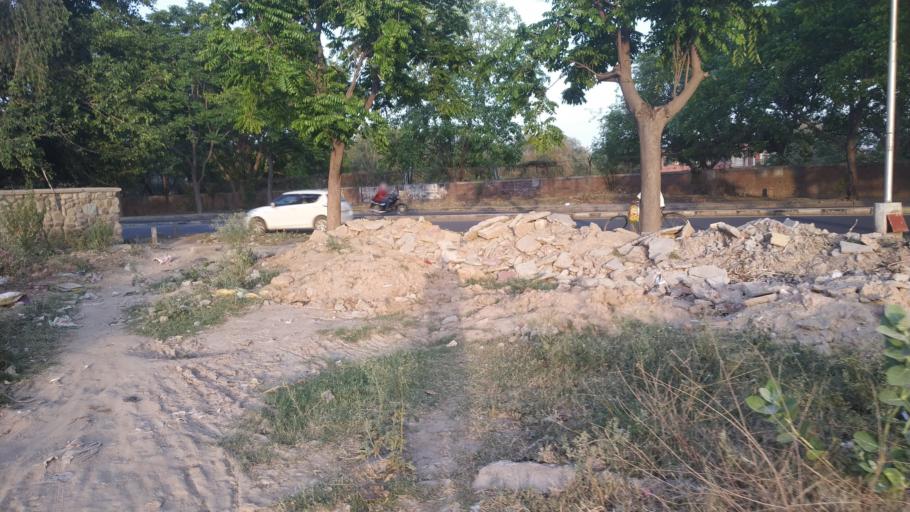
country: IN
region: Punjab
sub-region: Ajitgarh
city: Mohali
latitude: 30.6853
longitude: 76.7310
